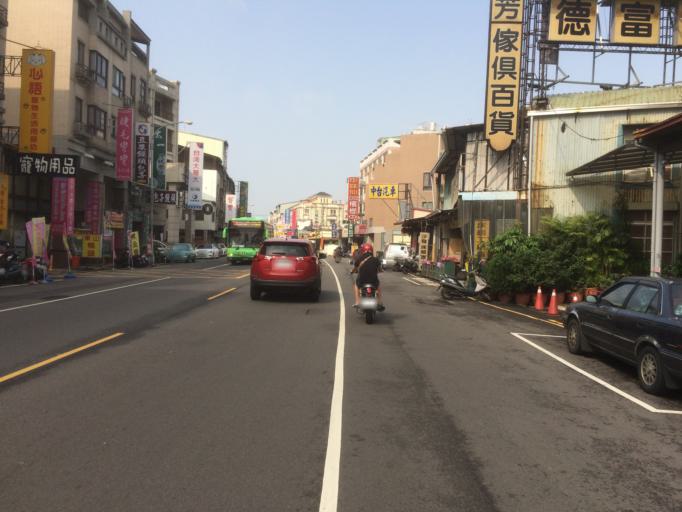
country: TW
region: Taiwan
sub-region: Taichung City
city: Taichung
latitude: 24.1721
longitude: 120.7109
